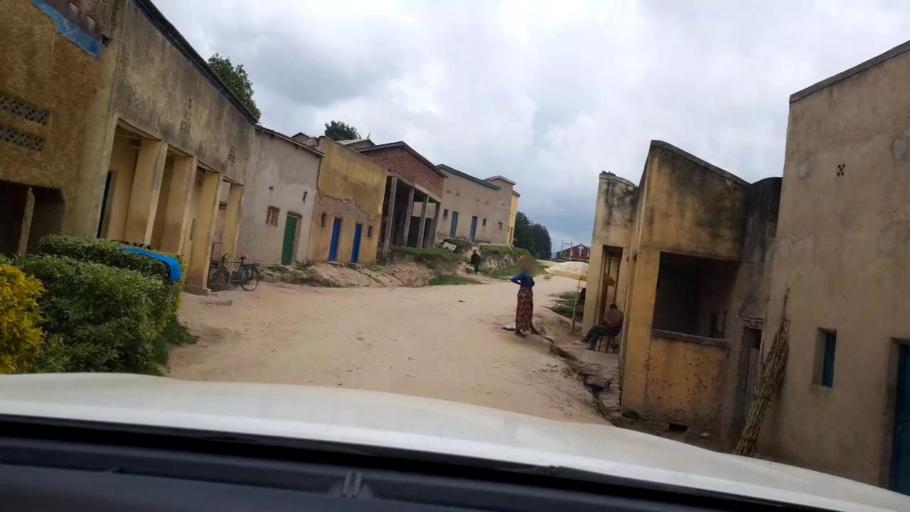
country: RW
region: Western Province
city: Kibuye
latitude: -1.8342
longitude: 29.5455
